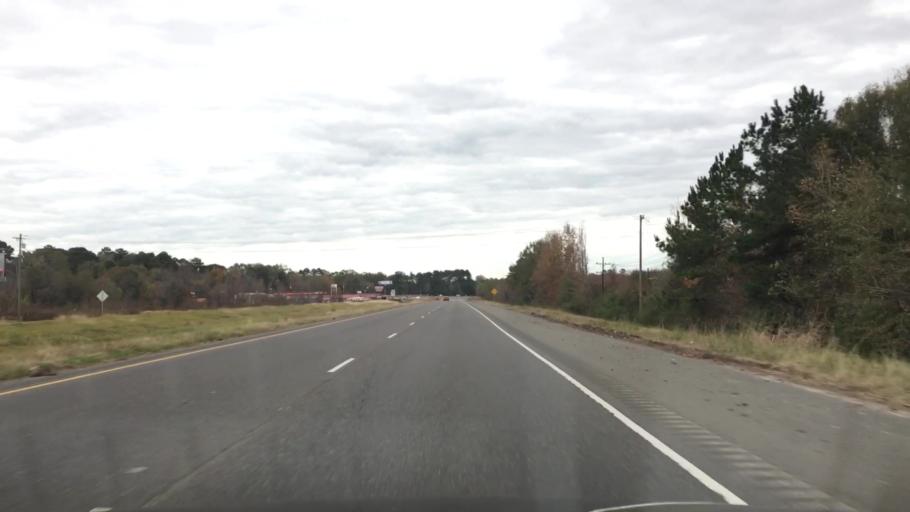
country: US
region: Louisiana
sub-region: Vernon Parish
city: New Llano
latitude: 31.1067
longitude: -93.2707
